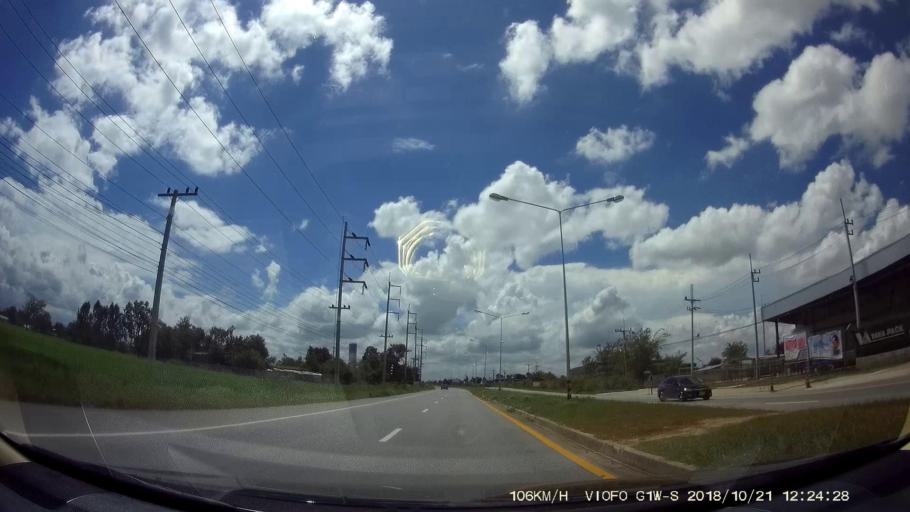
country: TH
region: Nakhon Ratchasima
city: Dan Khun Thot
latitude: 15.2328
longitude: 101.7830
